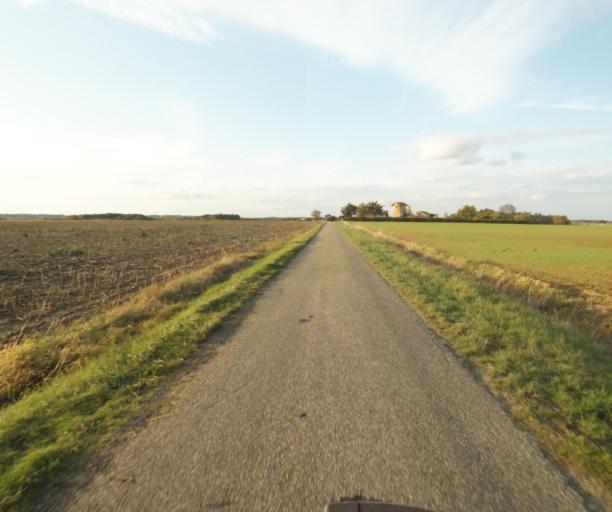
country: FR
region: Midi-Pyrenees
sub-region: Departement du Tarn-et-Garonne
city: Verdun-sur-Garonne
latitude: 43.8294
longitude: 1.1603
